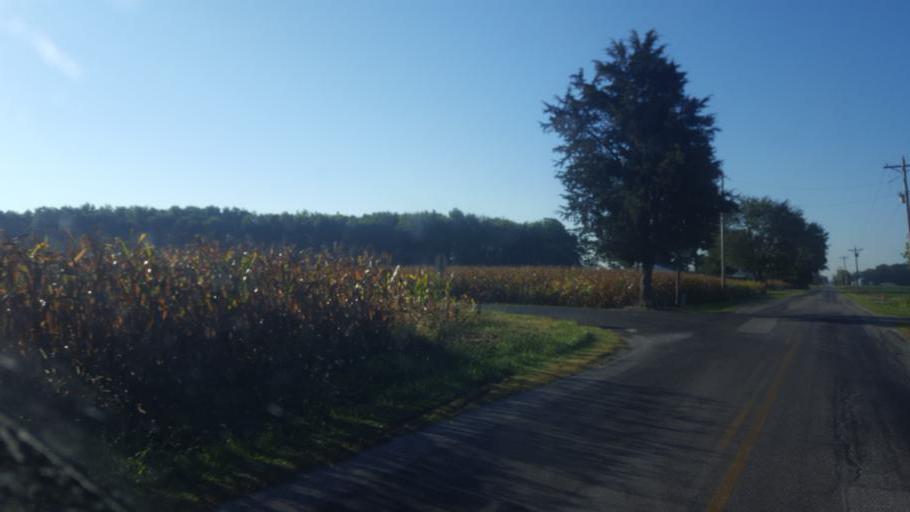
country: US
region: Ohio
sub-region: Morrow County
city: Cardington
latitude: 40.5505
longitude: -82.9957
